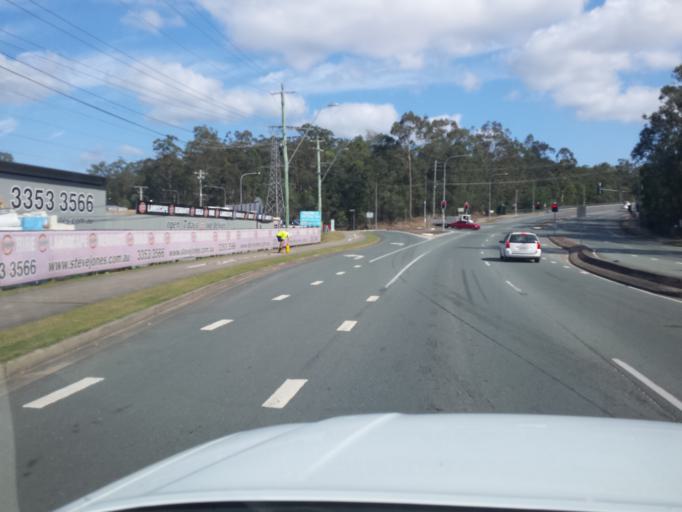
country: AU
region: Queensland
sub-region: Brisbane
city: Everton Park
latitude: -27.3812
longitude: 152.9820
